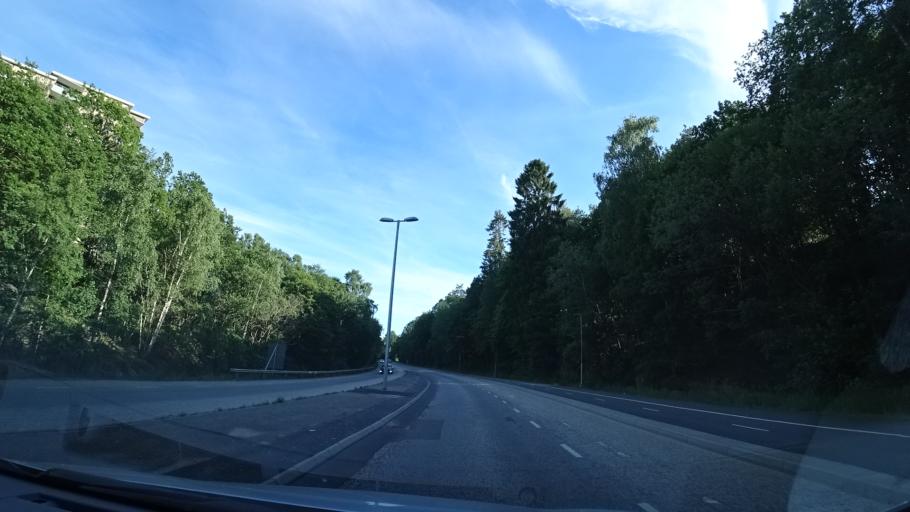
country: SE
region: Vaestra Goetaland
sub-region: Goteborg
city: Billdal
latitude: 57.5970
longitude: 11.9483
